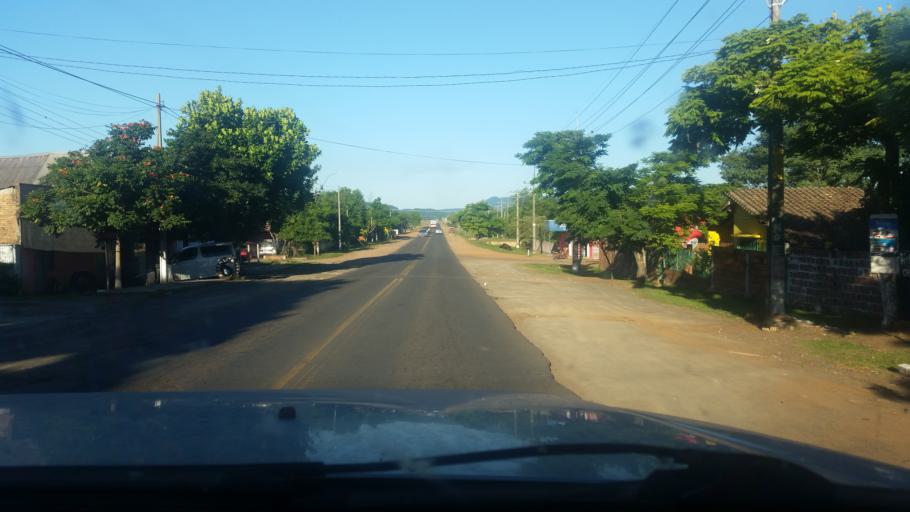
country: PY
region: Guaira
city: Mbocayaty
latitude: -25.7172
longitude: -56.4072
